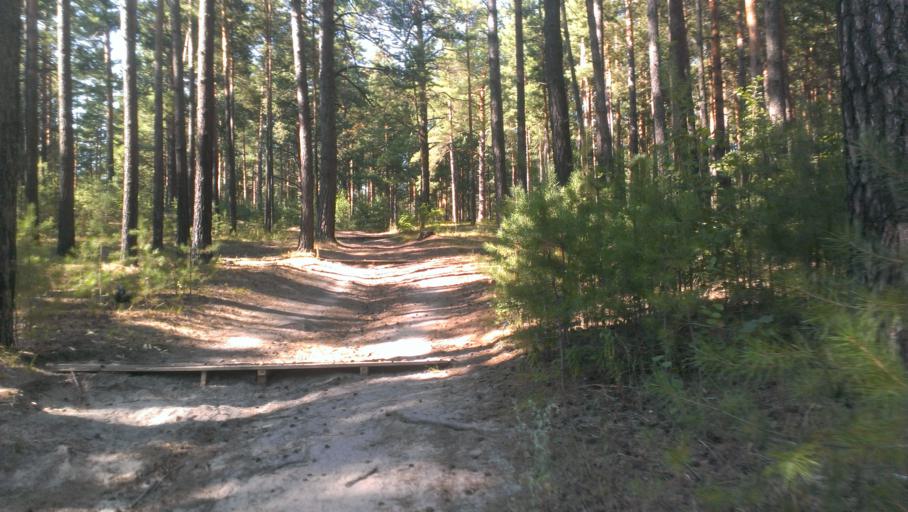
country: RU
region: Altai Krai
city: Novosilikatnyy
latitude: 53.3162
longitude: 83.6840
